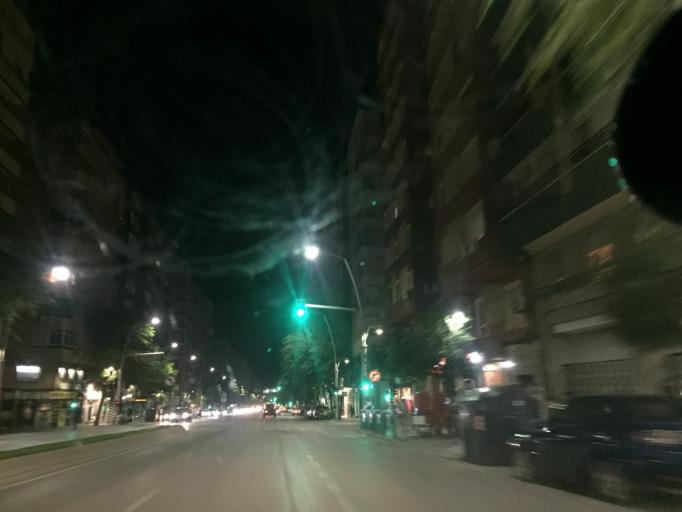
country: ES
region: Andalusia
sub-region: Provincia de Jaen
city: Jaen
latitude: 37.7778
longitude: -3.7997
